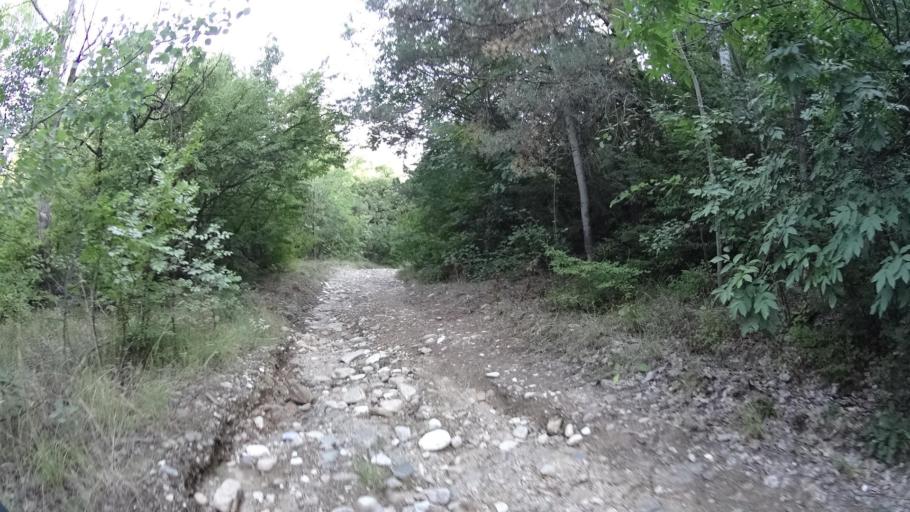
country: BG
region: Plovdiv
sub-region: Obshtina Plovdiv
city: Plovdiv
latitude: 42.0561
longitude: 24.6940
